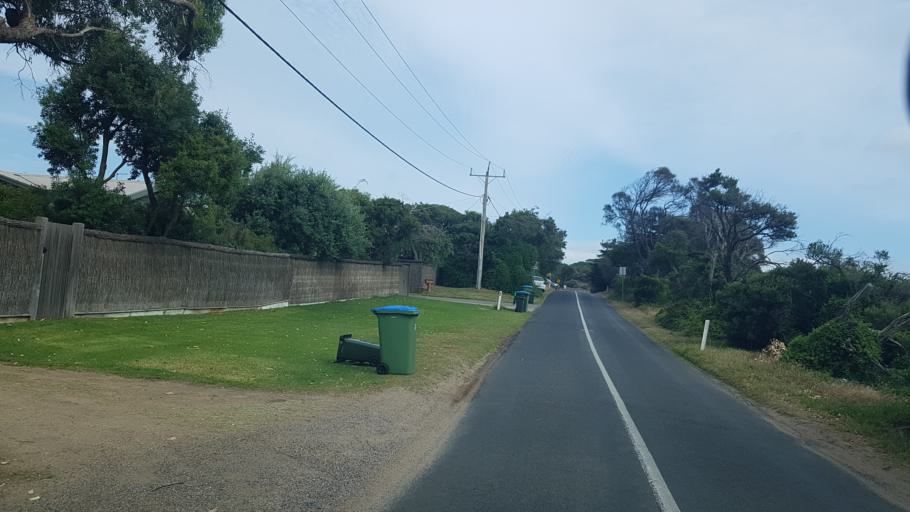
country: AU
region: Victoria
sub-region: Mornington Peninsula
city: Sorrento
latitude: -38.3283
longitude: 144.7063
